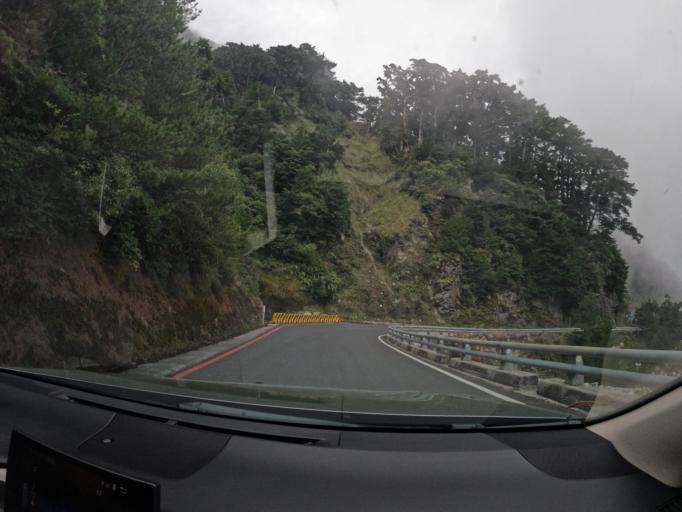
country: TW
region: Taiwan
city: Lugu
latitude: 23.2663
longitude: 120.9774
